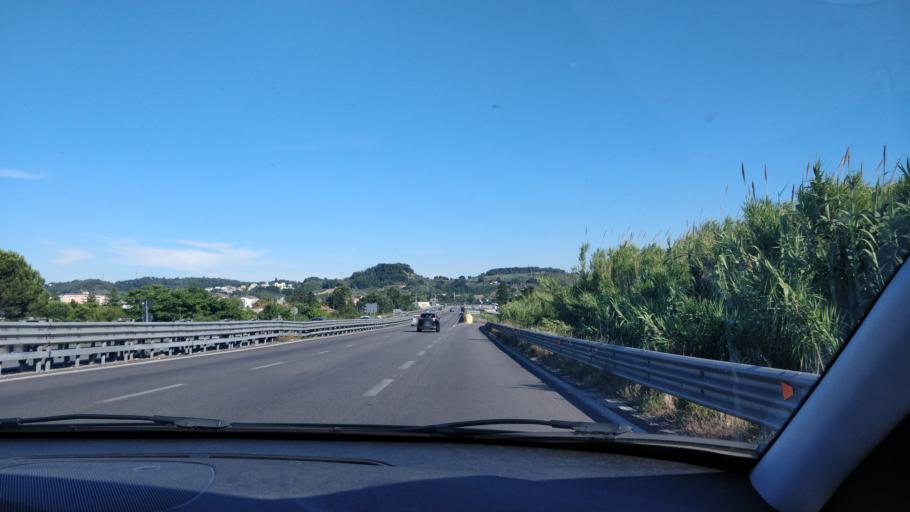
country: IT
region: Abruzzo
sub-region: Provincia di Pescara
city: Villa Raspa
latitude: 42.4439
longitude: 14.1904
